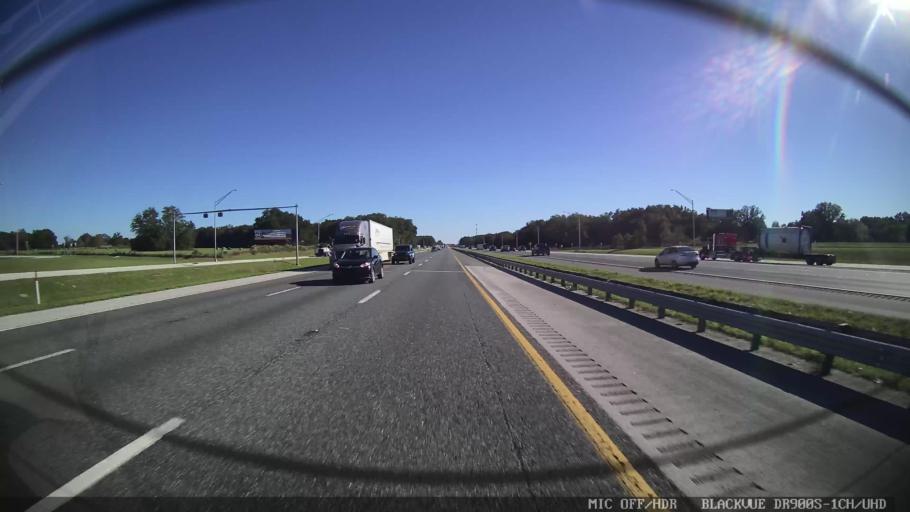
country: US
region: Florida
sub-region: Marion County
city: Belleview
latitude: 28.9918
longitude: -82.1419
